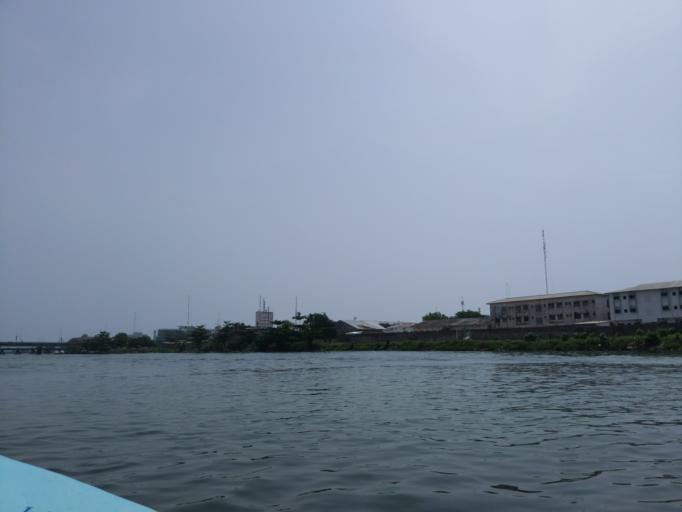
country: BJ
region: Littoral
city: Cotonou
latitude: 6.3629
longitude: 2.4393
